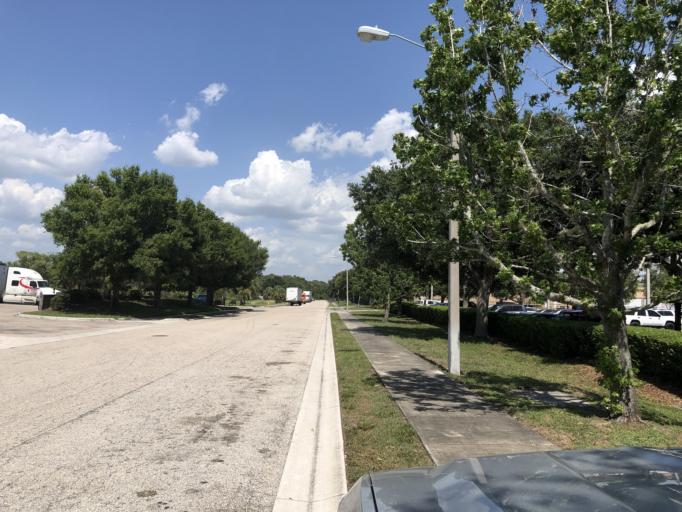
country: US
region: Florida
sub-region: Manatee County
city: Memphis
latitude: 27.5804
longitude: -82.5377
